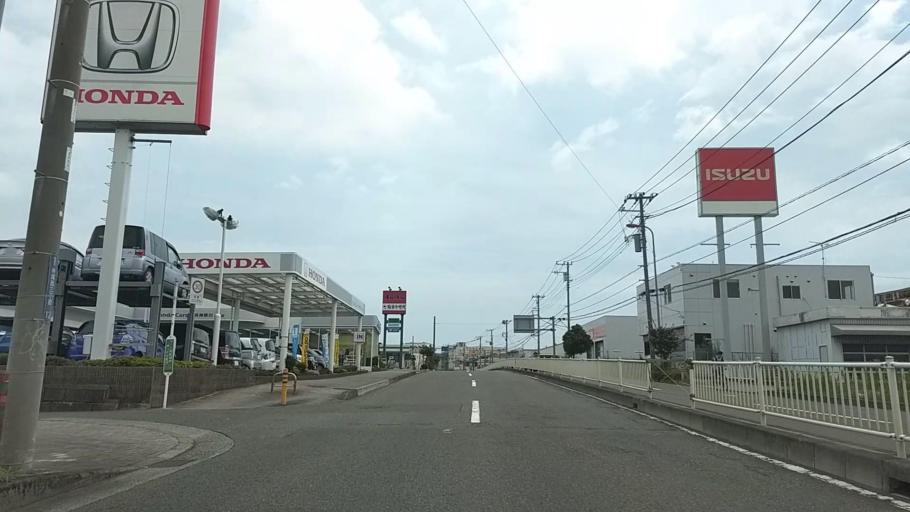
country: JP
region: Kanagawa
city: Minami-rinkan
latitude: 35.4544
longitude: 139.4175
